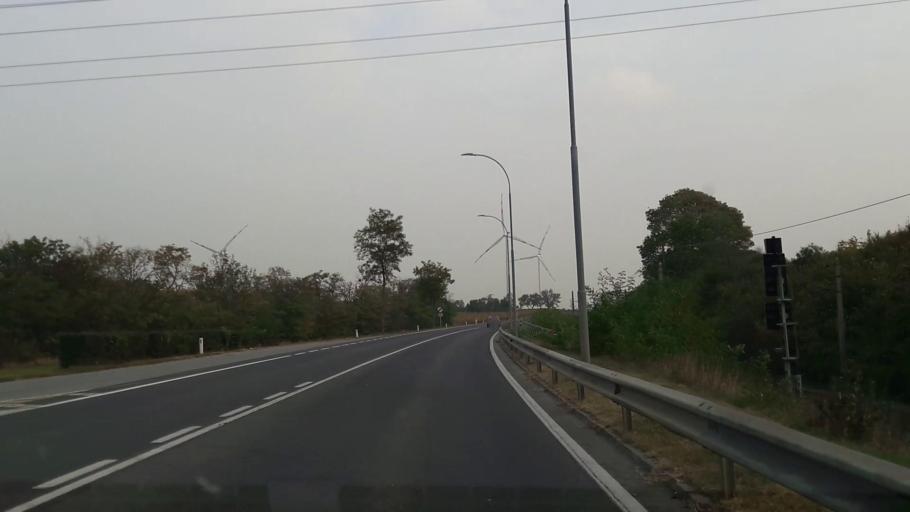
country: AT
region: Burgenland
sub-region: Politischer Bezirk Neusiedl am See
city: Bruckneudorf
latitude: 48.0159
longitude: 16.8090
